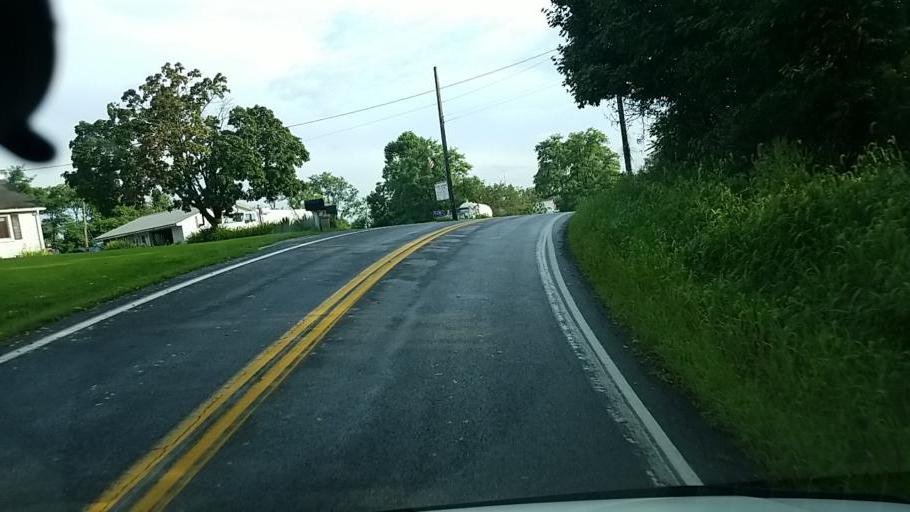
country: US
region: Pennsylvania
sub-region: Cumberland County
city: Newville
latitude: 40.2107
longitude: -77.4710
